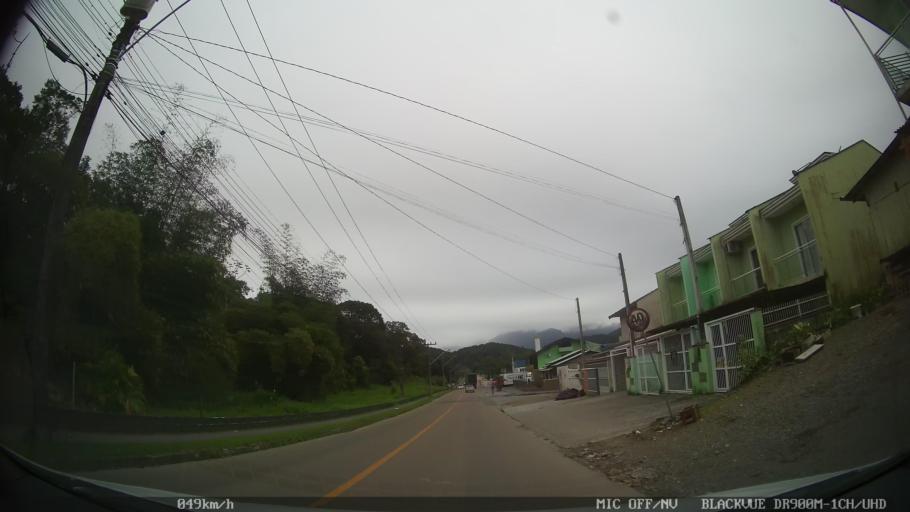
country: BR
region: Santa Catarina
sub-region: Joinville
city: Joinville
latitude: -26.2778
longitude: -48.9147
